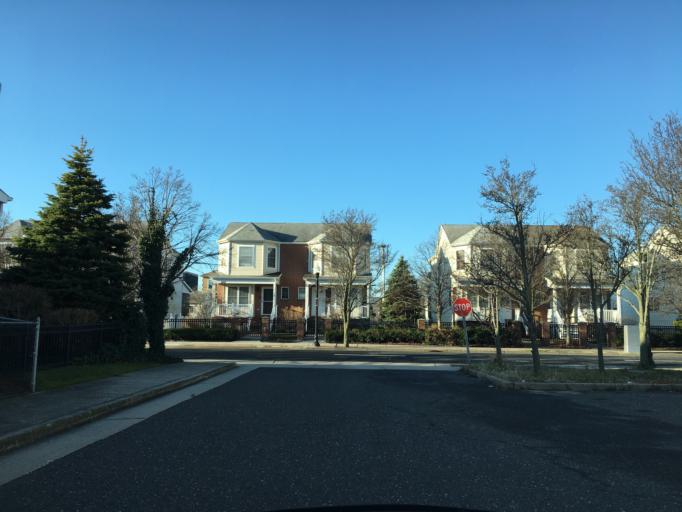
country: US
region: New Jersey
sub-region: Atlantic County
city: Atlantic City
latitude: 39.3667
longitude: -74.4244
